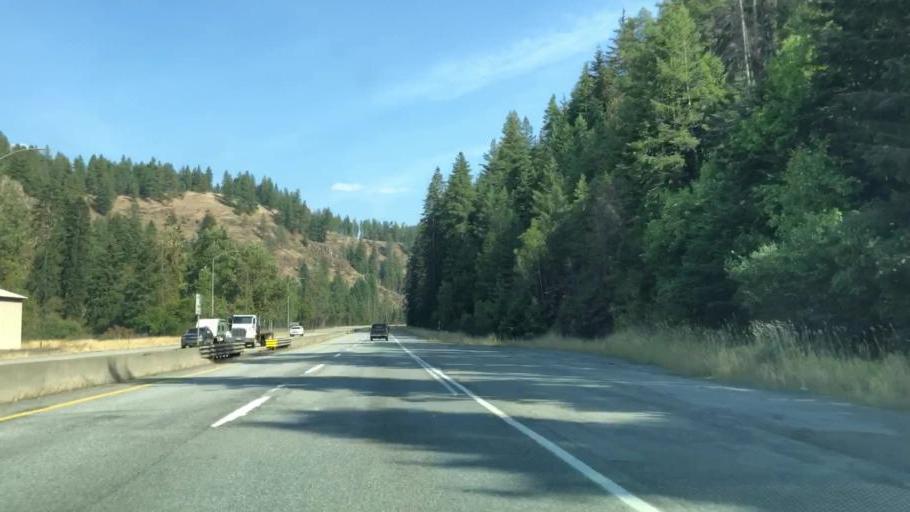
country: US
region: Idaho
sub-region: Kootenai County
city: Coeur d'Alene
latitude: 47.6306
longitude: -116.6088
